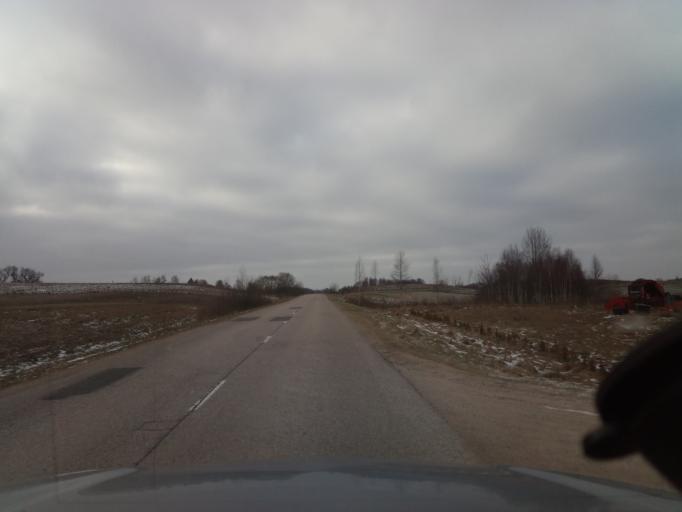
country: LT
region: Alytaus apskritis
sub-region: Alytaus rajonas
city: Daugai
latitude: 54.3501
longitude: 24.3224
